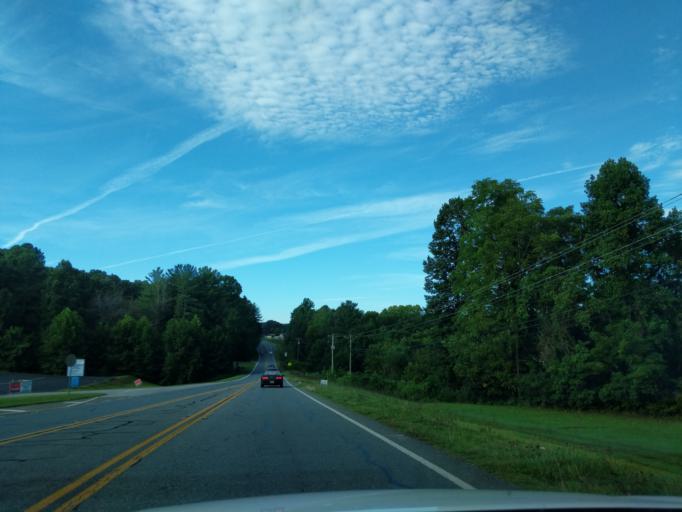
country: US
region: Georgia
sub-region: Fannin County
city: McCaysville
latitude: 34.9262
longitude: -84.3758
